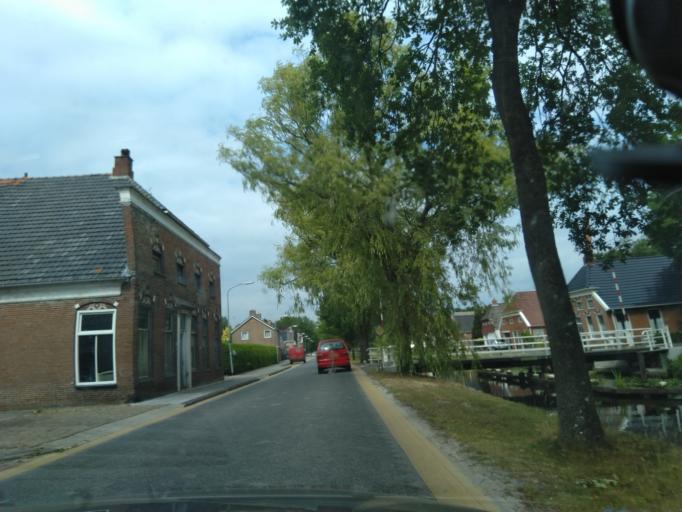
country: NL
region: Groningen
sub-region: Gemeente Pekela
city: Oude Pekela
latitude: 53.0900
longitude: 6.9842
